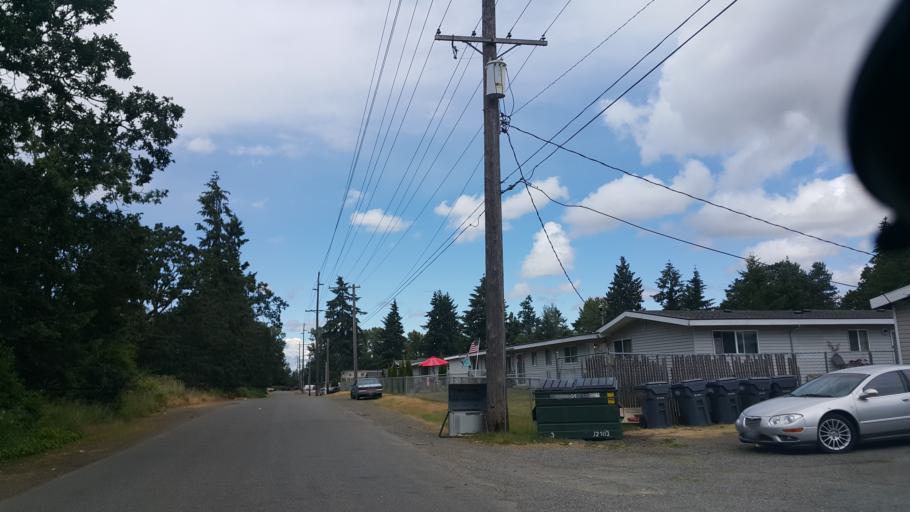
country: US
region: Washington
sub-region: Pierce County
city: McChord Air Force Base
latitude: 47.1397
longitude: -122.4993
